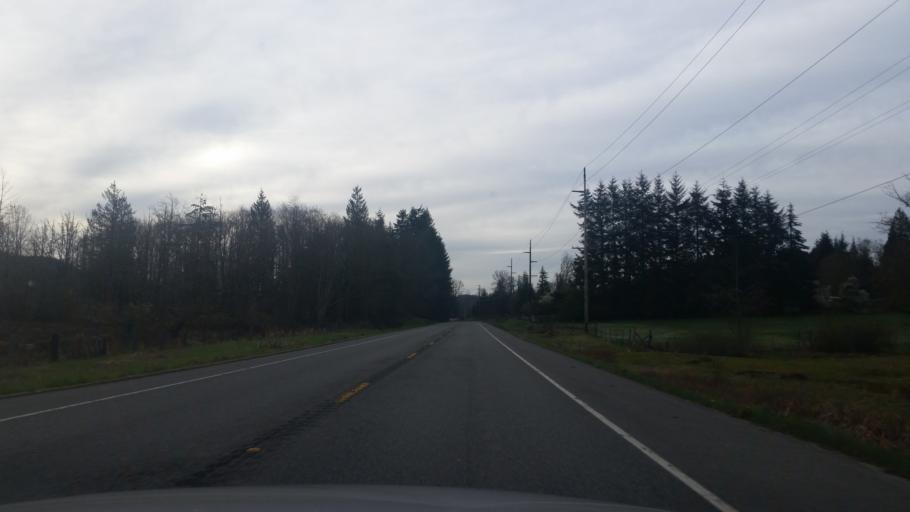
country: US
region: Washington
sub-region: Pierce County
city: Eatonville
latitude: 46.7878
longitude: -122.2585
